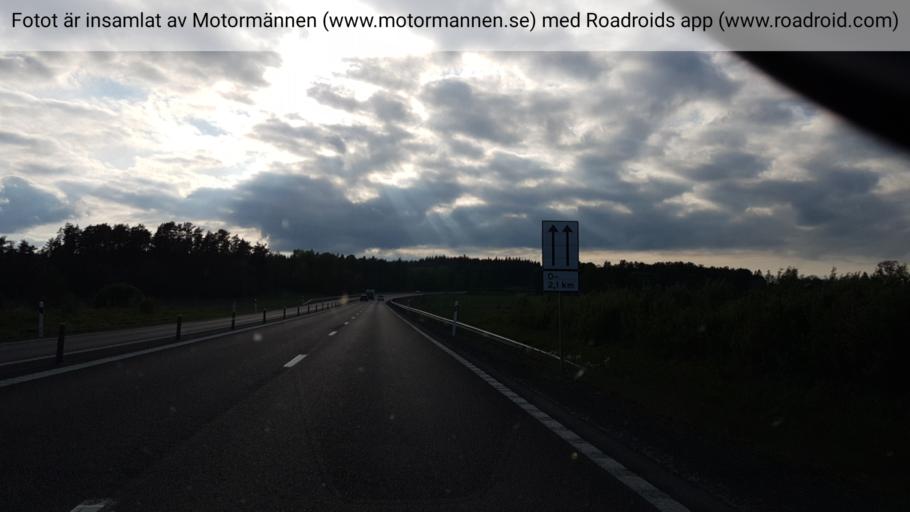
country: SE
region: Joenkoeping
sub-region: Jonkopings Kommun
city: Tenhult
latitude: 57.7212
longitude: 14.3633
